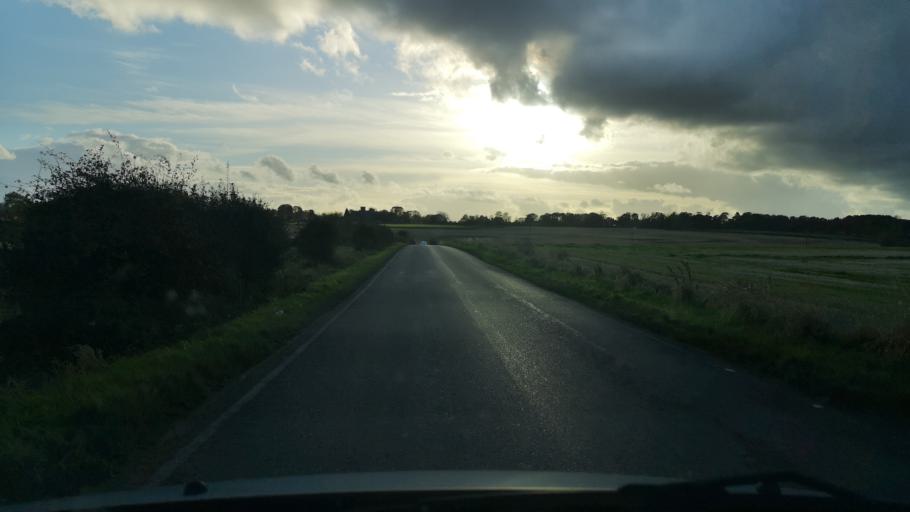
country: GB
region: England
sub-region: City and Borough of Wakefield
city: Darrington
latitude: 53.6669
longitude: -1.2937
